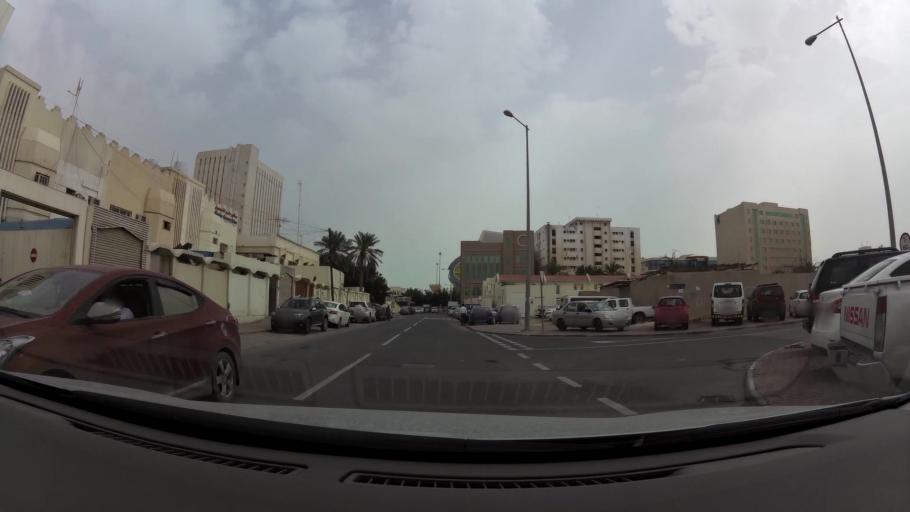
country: QA
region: Baladiyat ad Dawhah
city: Doha
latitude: 25.2655
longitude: 51.5504
